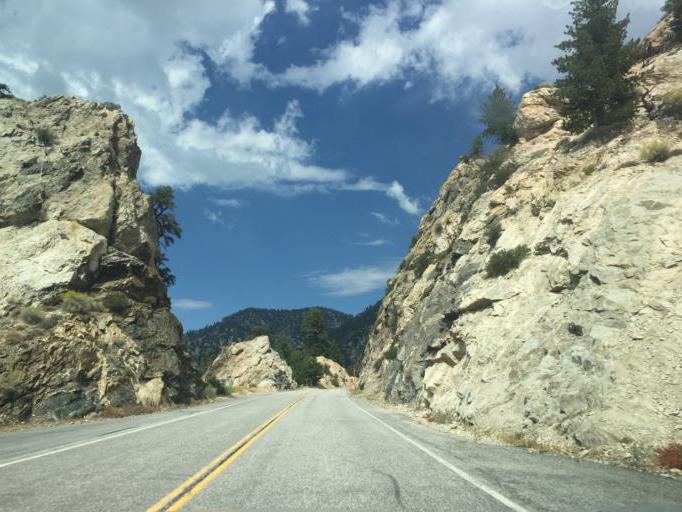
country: US
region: California
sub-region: Los Angeles County
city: Littlerock
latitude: 34.3583
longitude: -117.8770
